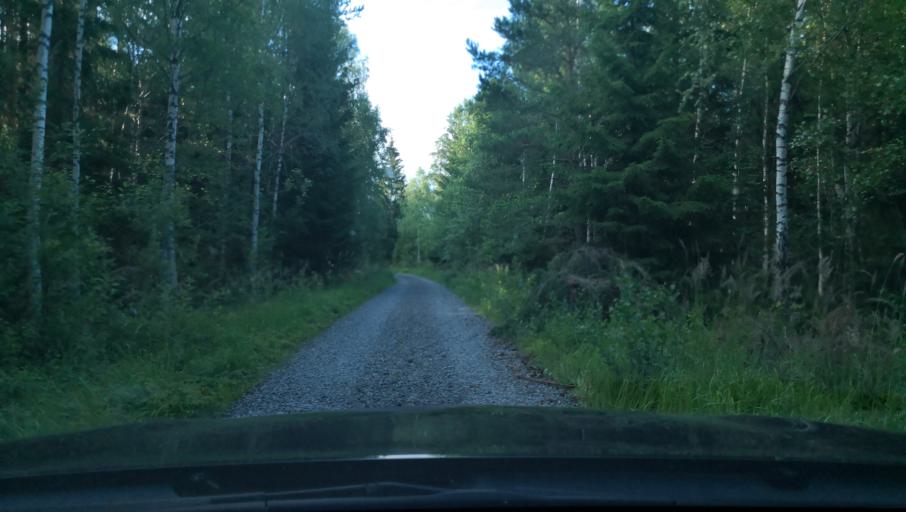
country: SE
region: Uppsala
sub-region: Osthammars Kommun
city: Osterbybruk
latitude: 60.0237
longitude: 17.9194
